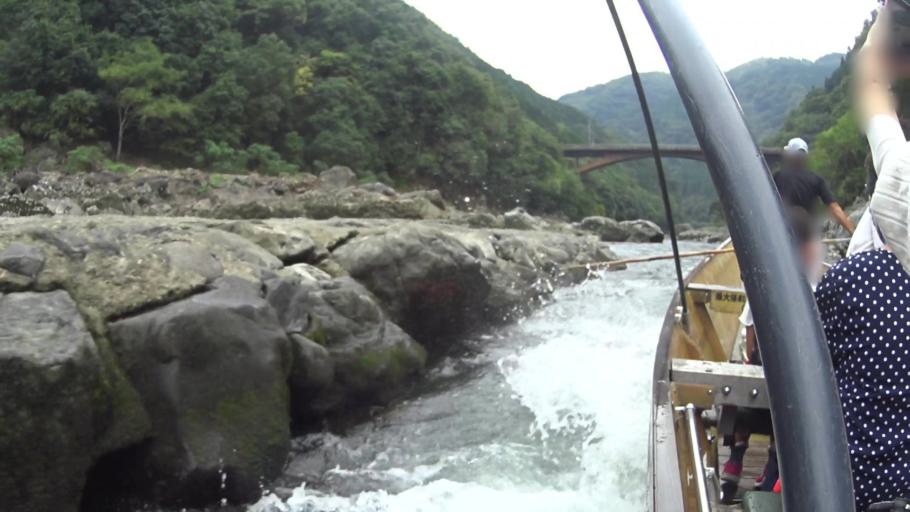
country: JP
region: Kyoto
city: Kameoka
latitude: 35.0228
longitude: 135.6213
